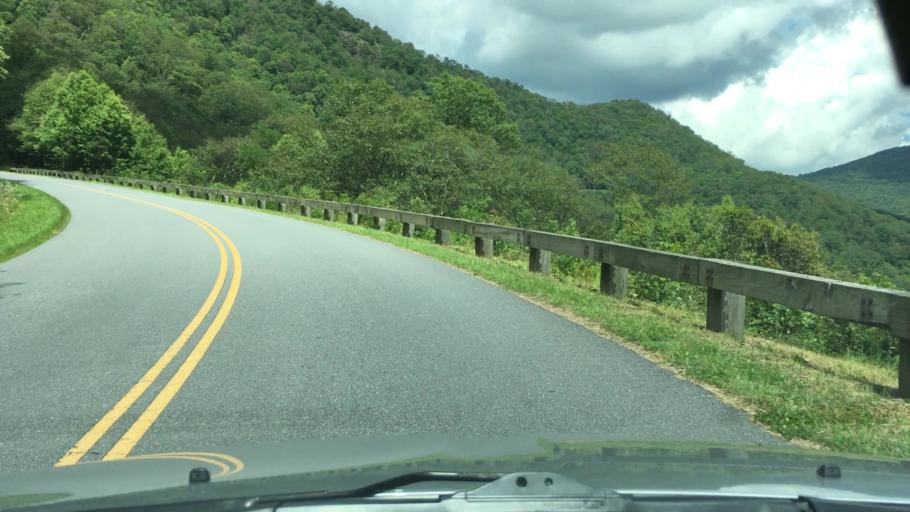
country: US
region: North Carolina
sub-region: Buncombe County
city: Swannanoa
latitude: 35.6787
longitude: -82.4170
